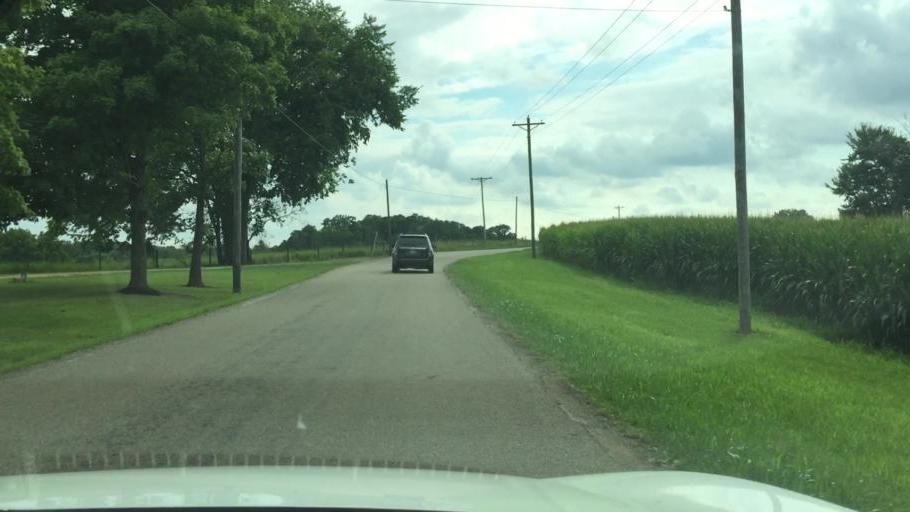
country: US
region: Ohio
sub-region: Champaign County
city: Mechanicsburg
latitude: 40.0173
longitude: -83.6291
